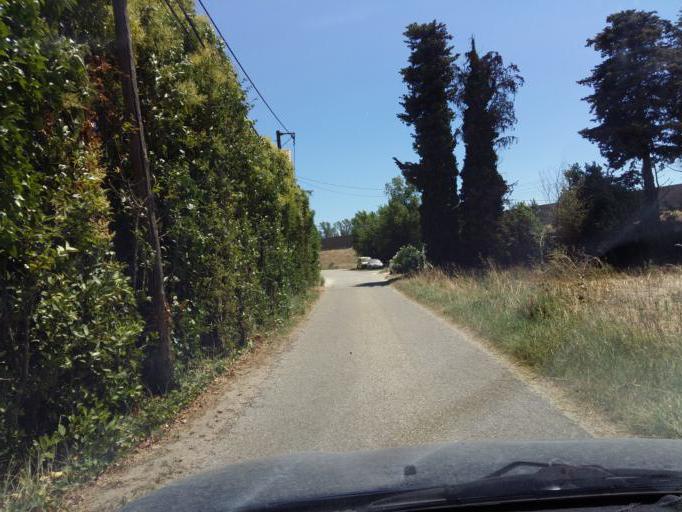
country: FR
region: Provence-Alpes-Cote d'Azur
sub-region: Departement du Vaucluse
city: Mornas
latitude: 44.1675
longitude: 4.7323
